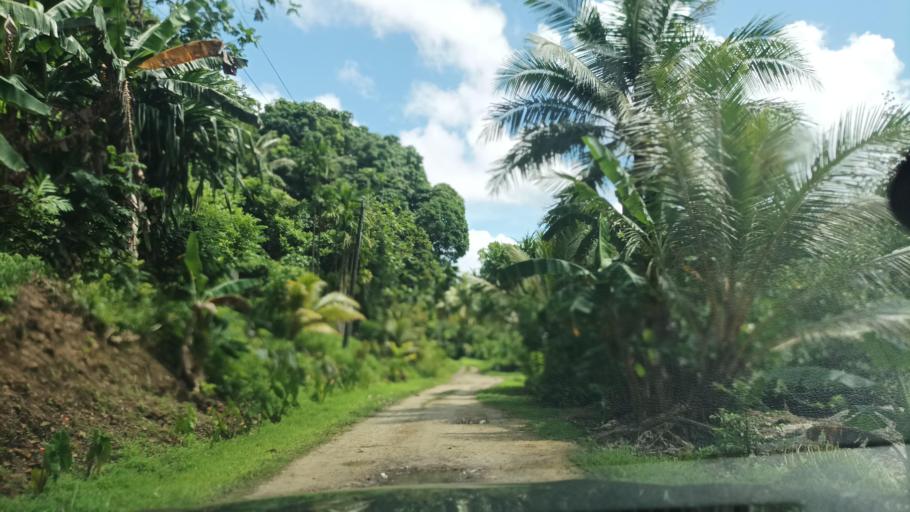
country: FM
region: Pohnpei
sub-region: Sokehs Municipality
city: Palikir - National Government Center
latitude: 6.9443
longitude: 158.1615
